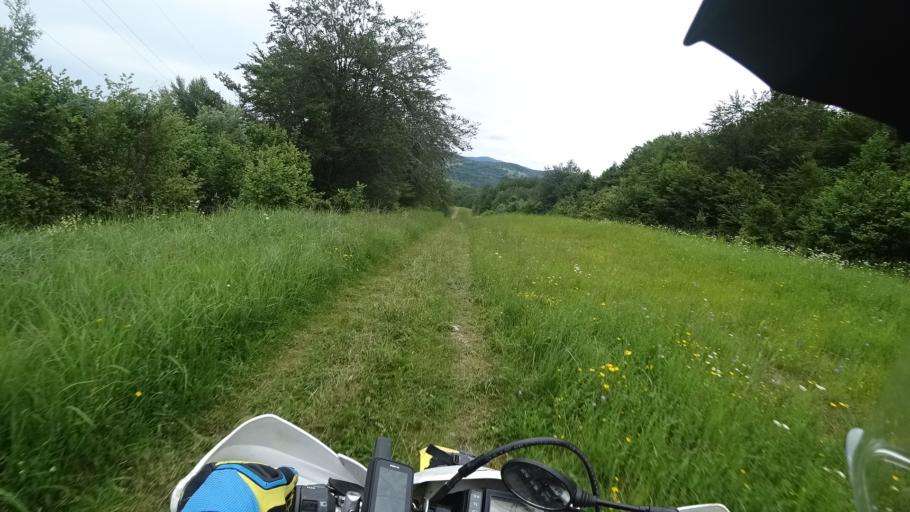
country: HR
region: Primorsko-Goranska
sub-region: Grad Delnice
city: Delnice
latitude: 45.3814
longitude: 14.8645
